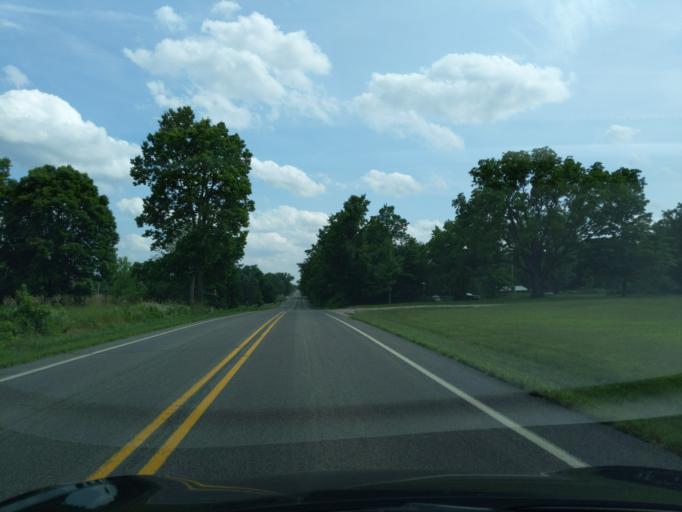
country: US
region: Michigan
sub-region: Eaton County
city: Dimondale
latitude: 42.6046
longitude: -84.6026
